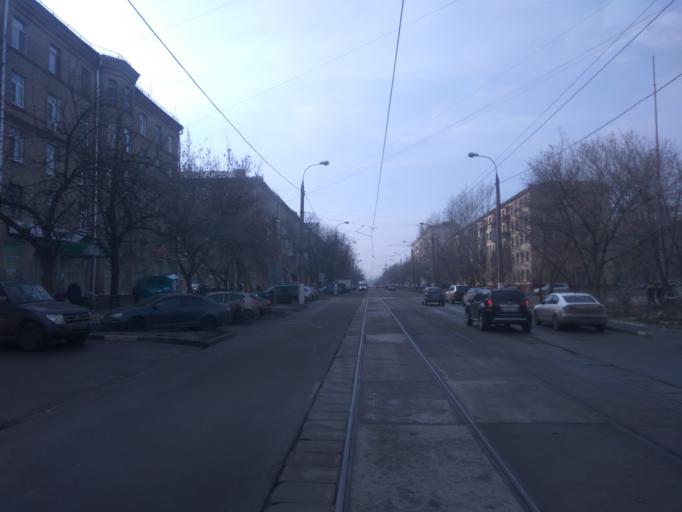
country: RU
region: Moscow
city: Kolomenskoye
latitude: 55.6841
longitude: 37.6863
